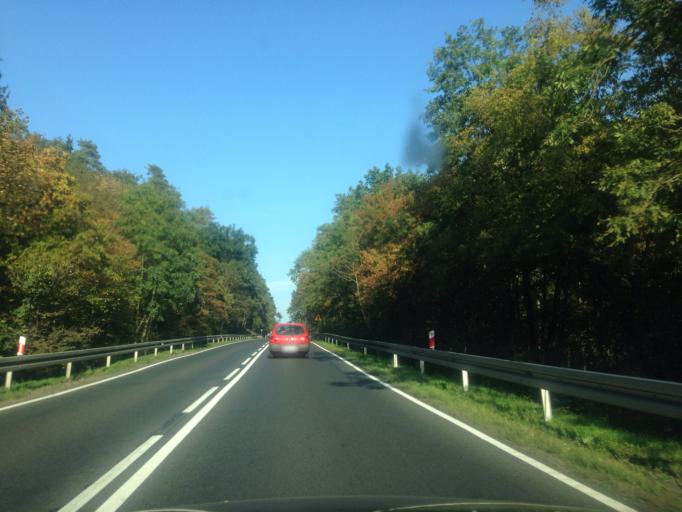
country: PL
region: Kujawsko-Pomorskie
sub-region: Powiat brodnicki
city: Brodnica
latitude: 53.2837
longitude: 19.4817
